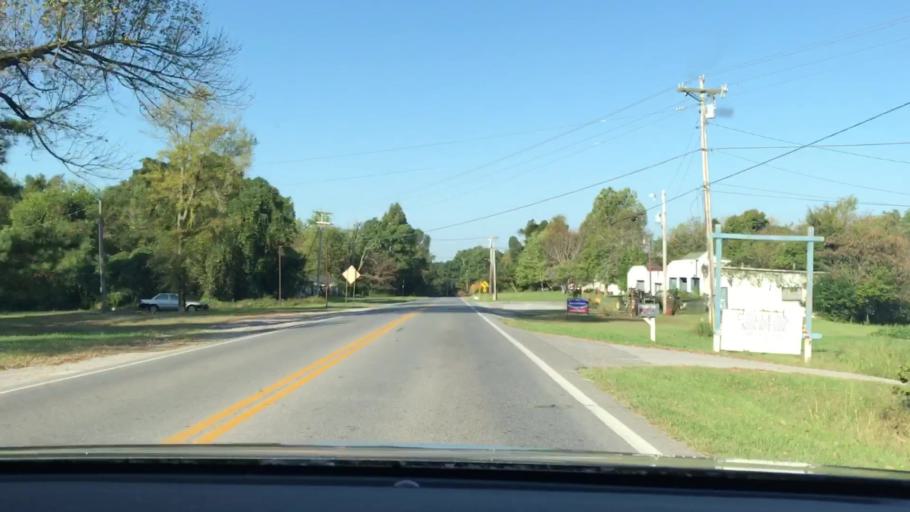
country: US
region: Kentucky
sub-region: Trigg County
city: Cadiz
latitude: 36.8112
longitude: -87.8946
